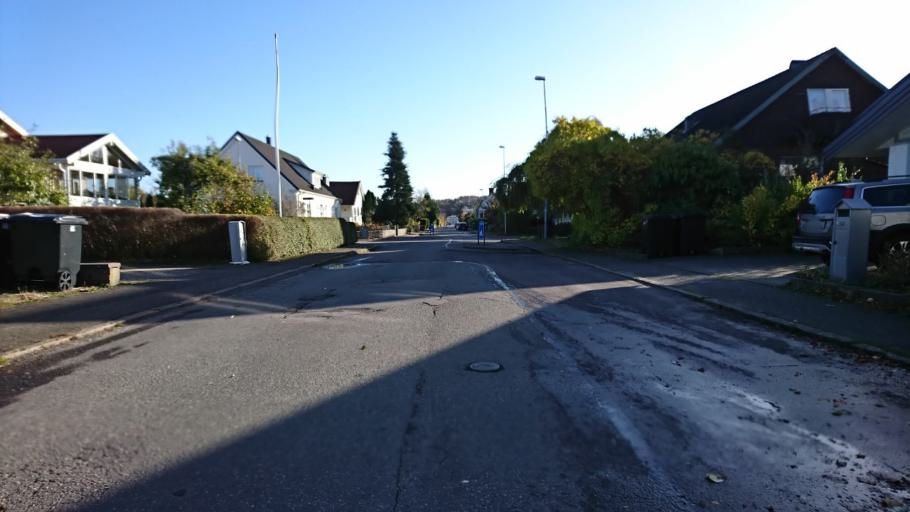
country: SE
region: Vaestra Goetaland
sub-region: Molndal
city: Moelndal
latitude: 57.6546
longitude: 11.9952
